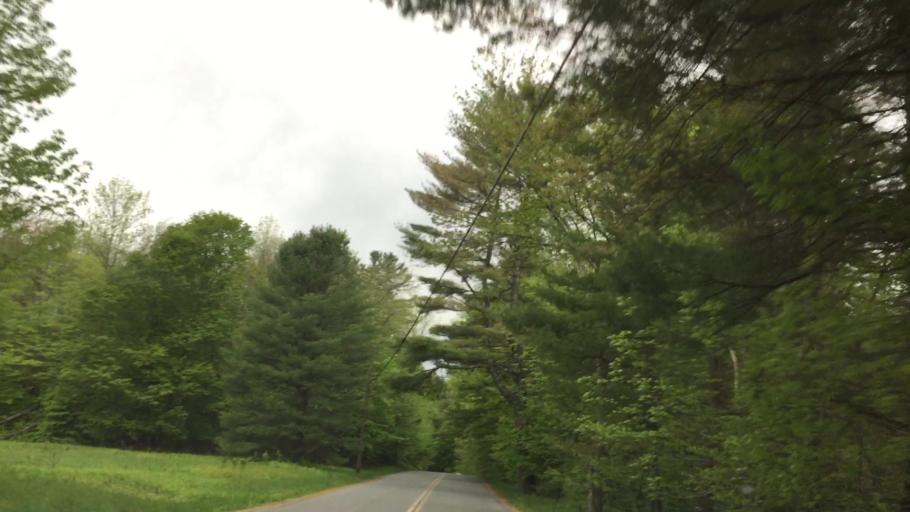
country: US
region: Massachusetts
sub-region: Berkshire County
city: Becket
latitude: 42.2766
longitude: -73.0370
